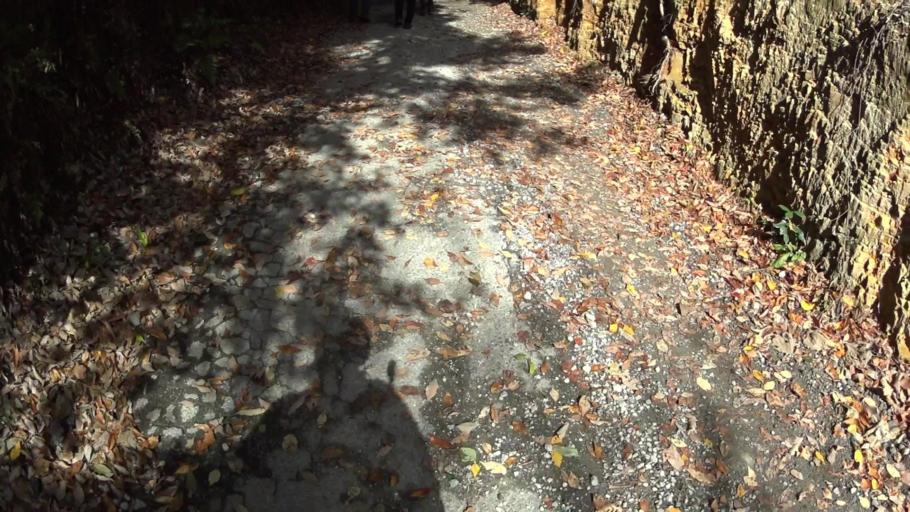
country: JP
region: Kyoto
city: Uji
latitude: 34.9469
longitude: 135.7908
